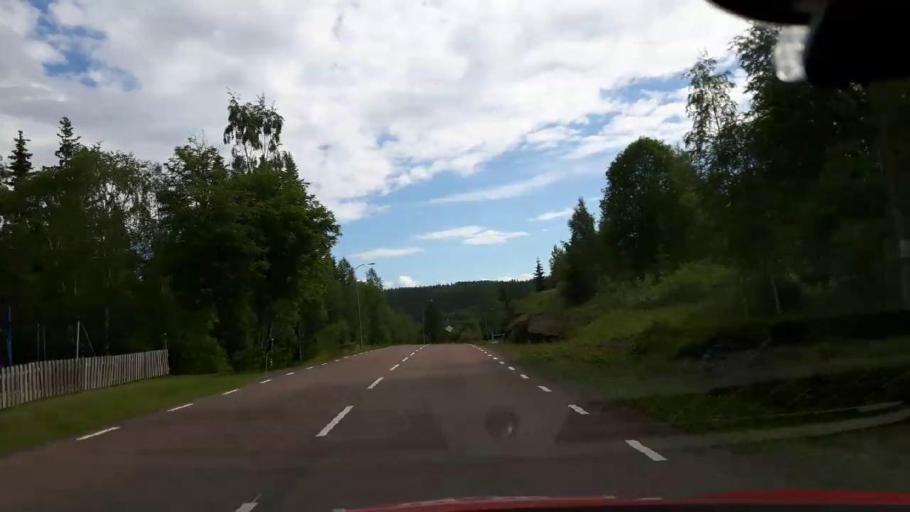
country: SE
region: Jaemtland
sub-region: Krokoms Kommun
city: Valla
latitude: 63.9113
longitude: 14.2162
